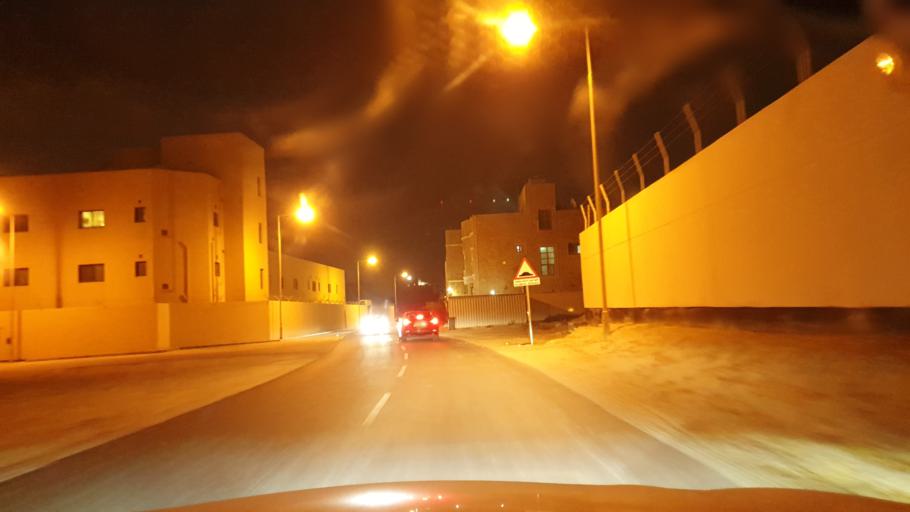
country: BH
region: Manama
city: Jidd Hafs
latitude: 26.1968
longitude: 50.4883
